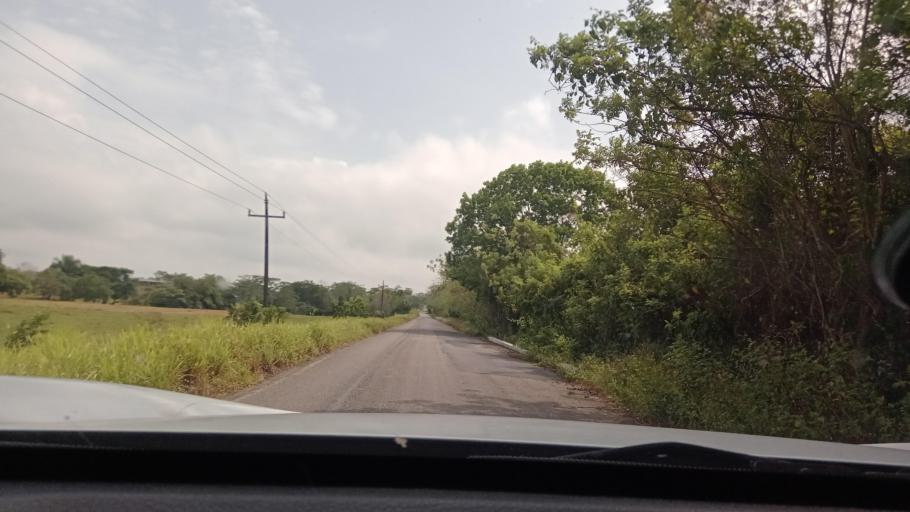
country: MX
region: Tabasco
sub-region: Huimanguillo
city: Francisco Rueda
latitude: 17.5611
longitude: -94.1172
